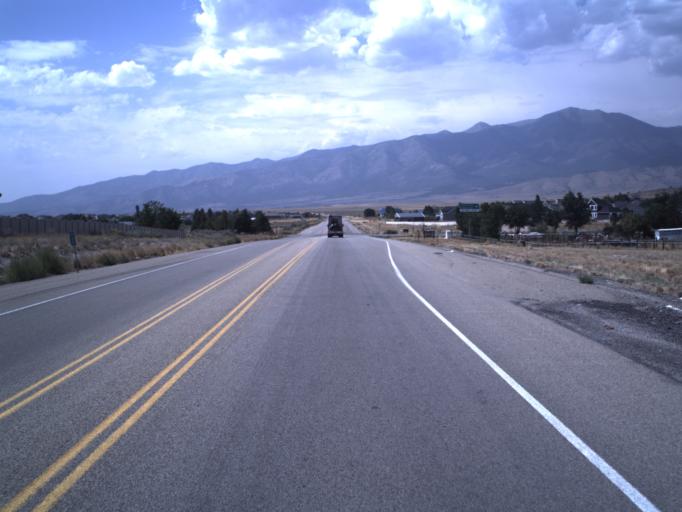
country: US
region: Utah
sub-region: Utah County
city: Eagle Mountain
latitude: 40.3787
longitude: -111.9987
